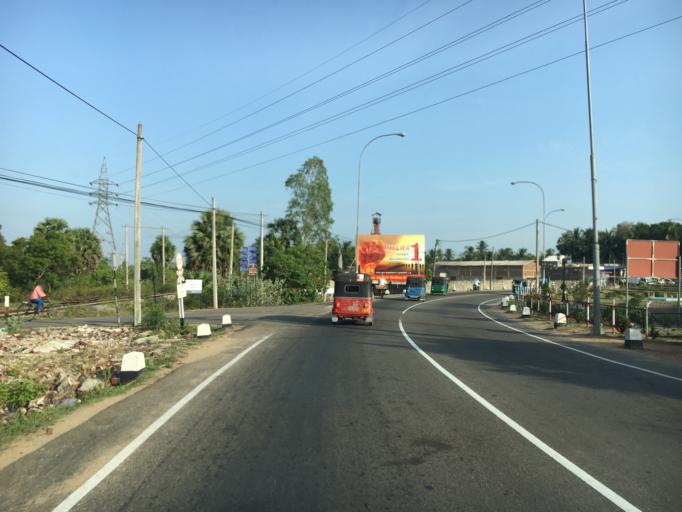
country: LK
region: Eastern Province
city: Eravur Town
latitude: 7.9227
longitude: 81.5139
